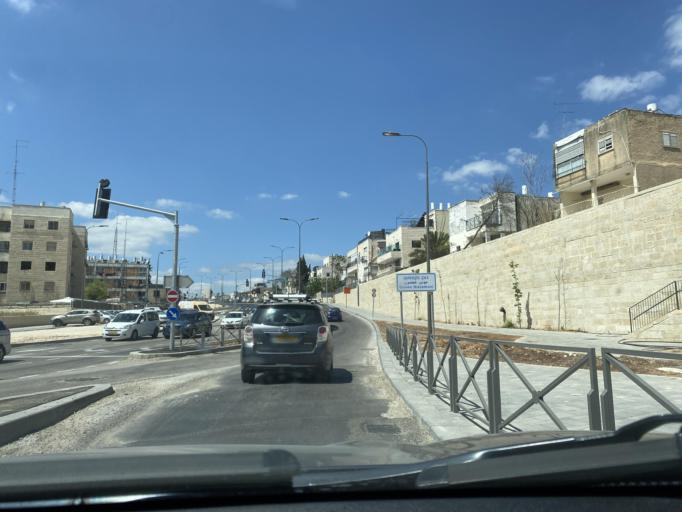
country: IL
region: Jerusalem
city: Jerusalem
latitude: 31.7535
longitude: 35.1998
